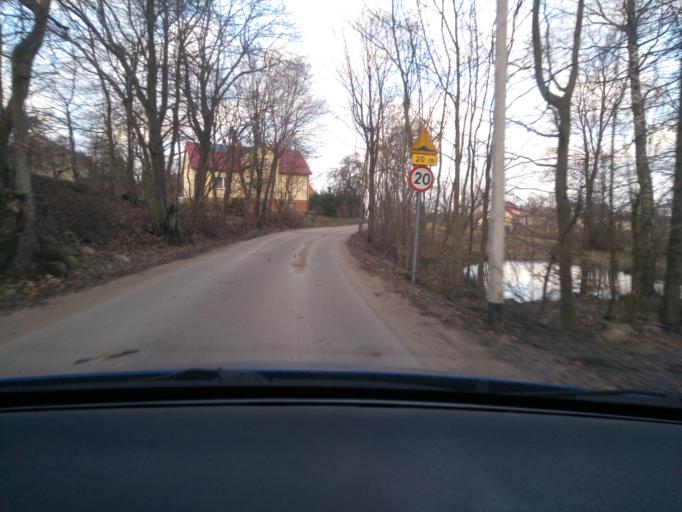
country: PL
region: Pomeranian Voivodeship
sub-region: Powiat kartuski
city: Przodkowo
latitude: 54.4161
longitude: 18.2790
